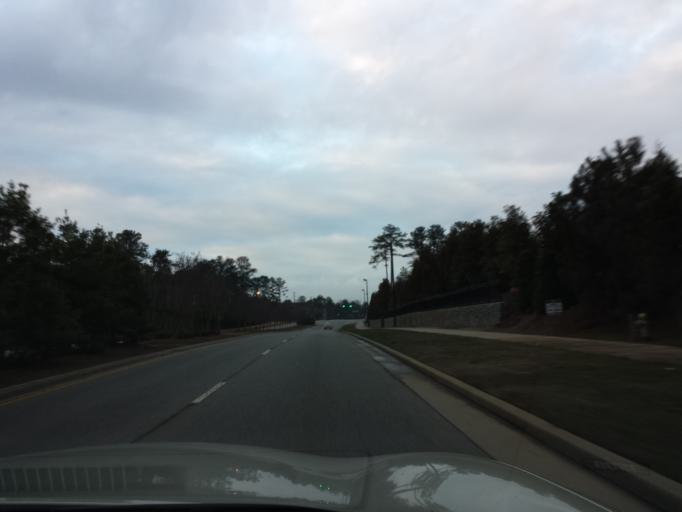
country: US
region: Georgia
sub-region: Fulton County
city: Alpharetta
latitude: 34.0645
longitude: -84.2836
